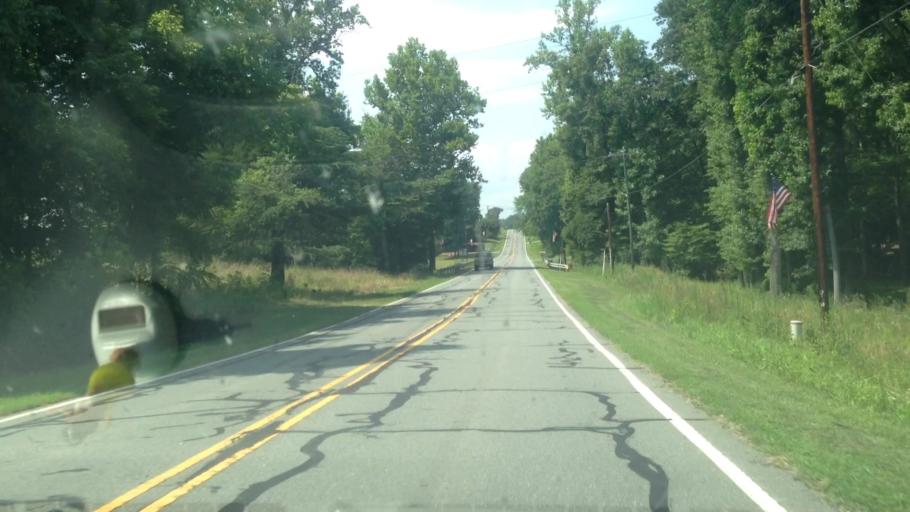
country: US
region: North Carolina
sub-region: Stokes County
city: Walnut Cove
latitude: 36.3320
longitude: -80.0482
